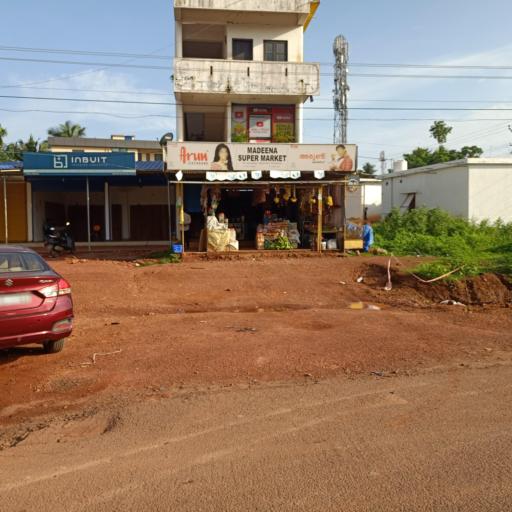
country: IN
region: Kerala
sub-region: Kasaragod District
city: Kasaragod
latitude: 12.5104
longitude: 75.0364
